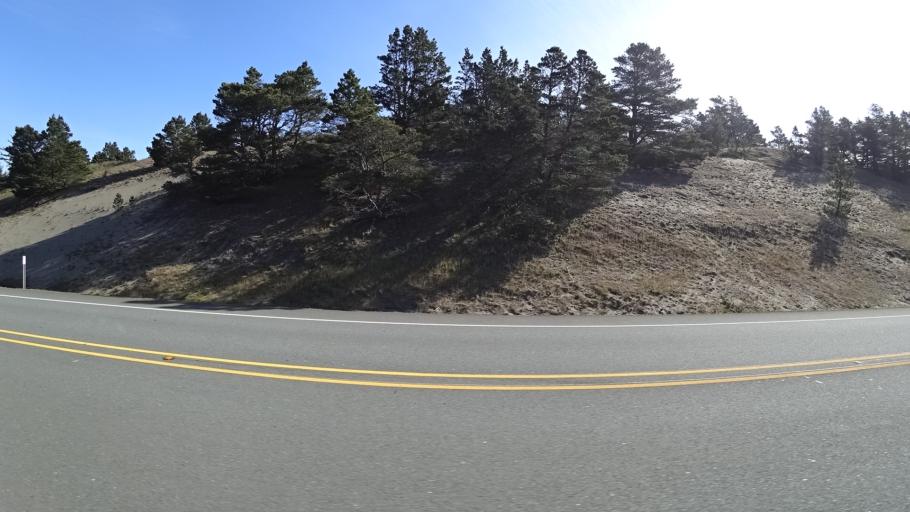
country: US
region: Oregon
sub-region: Curry County
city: Gold Beach
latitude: 42.2532
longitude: -124.3961
